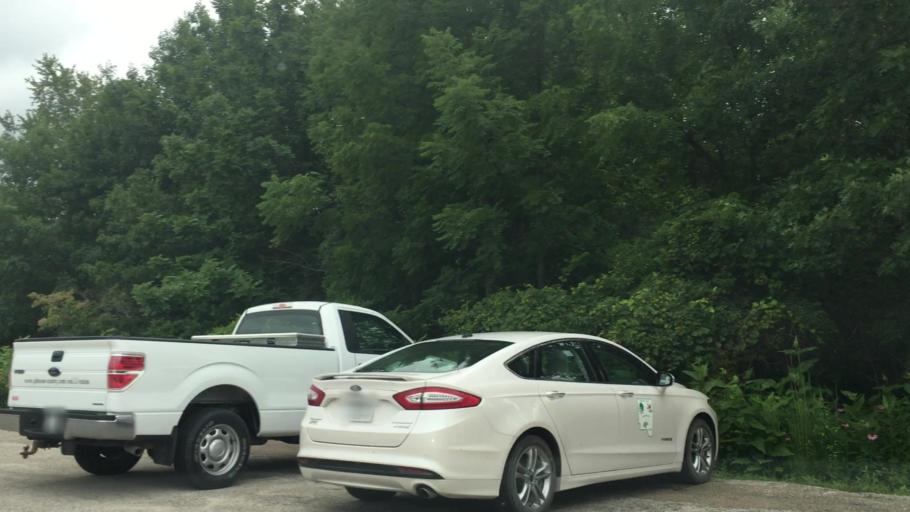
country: US
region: Iowa
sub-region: Johnson County
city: Tiffin
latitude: 41.7352
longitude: -91.7232
